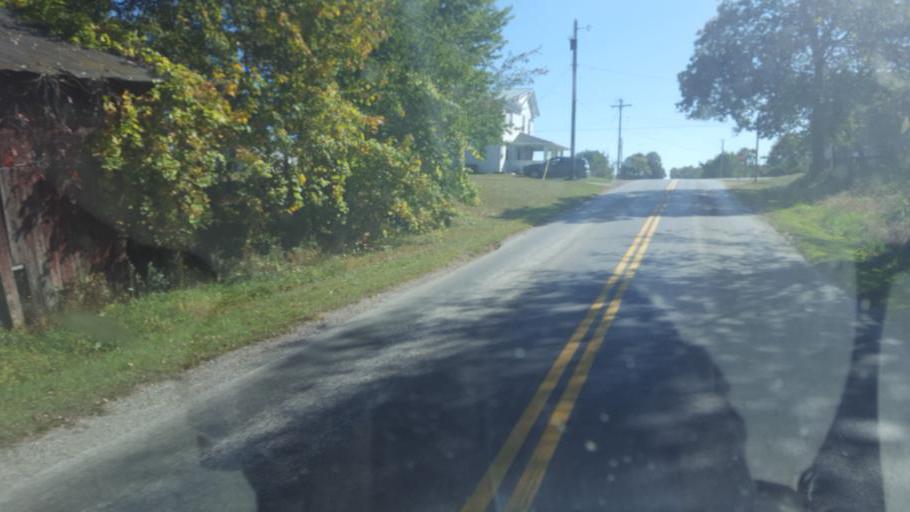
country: US
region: Ohio
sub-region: Wayne County
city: West Salem
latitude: 40.9748
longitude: -82.1629
